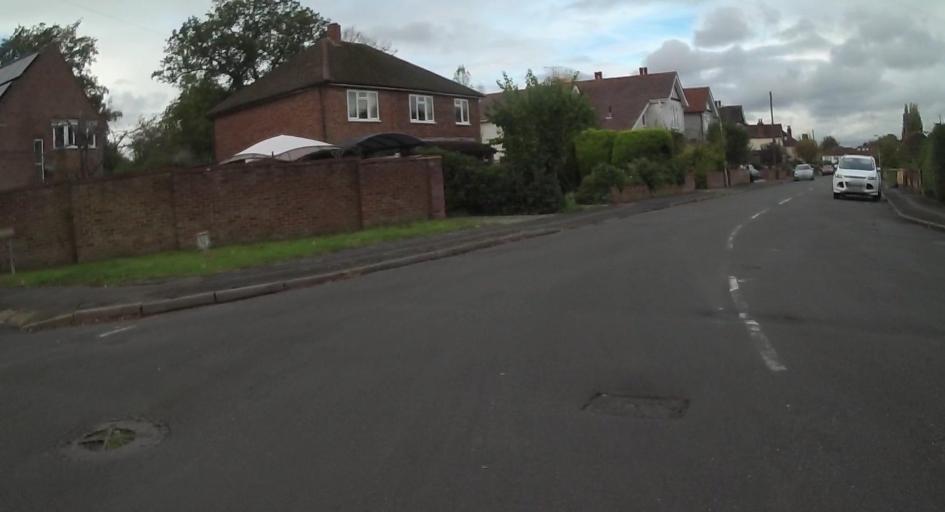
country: GB
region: England
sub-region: Hampshire
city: Farnborough
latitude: 51.2926
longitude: -0.7420
